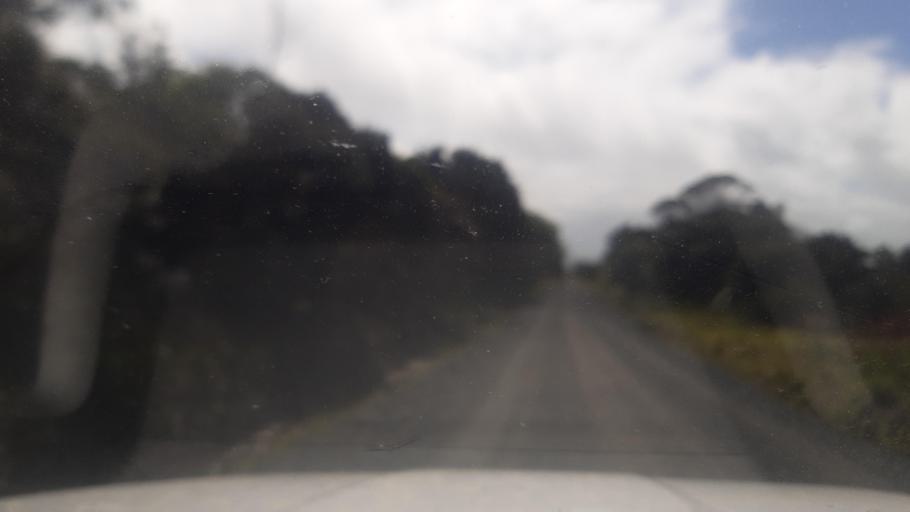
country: NZ
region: Northland
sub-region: Far North District
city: Kaitaia
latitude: -34.7433
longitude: 173.1063
